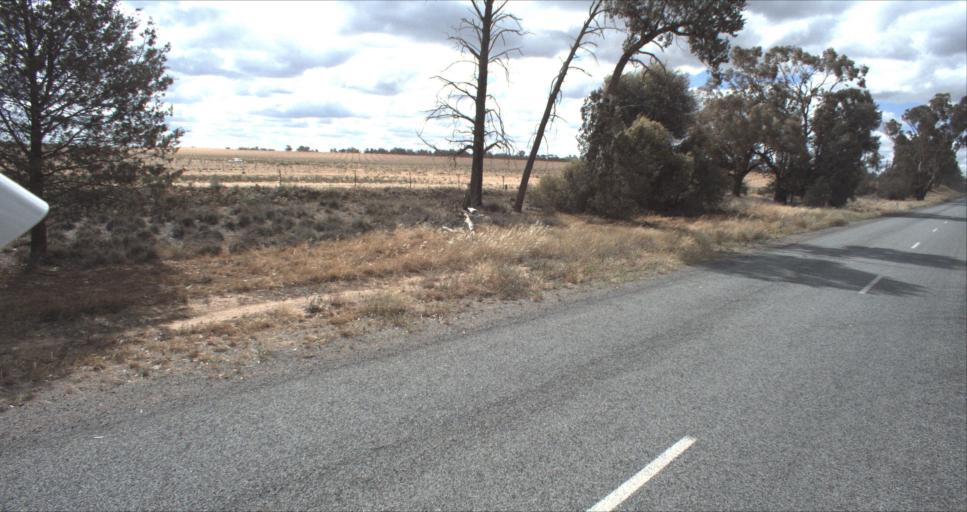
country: AU
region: New South Wales
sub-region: Leeton
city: Leeton
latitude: -34.6625
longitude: 146.3491
